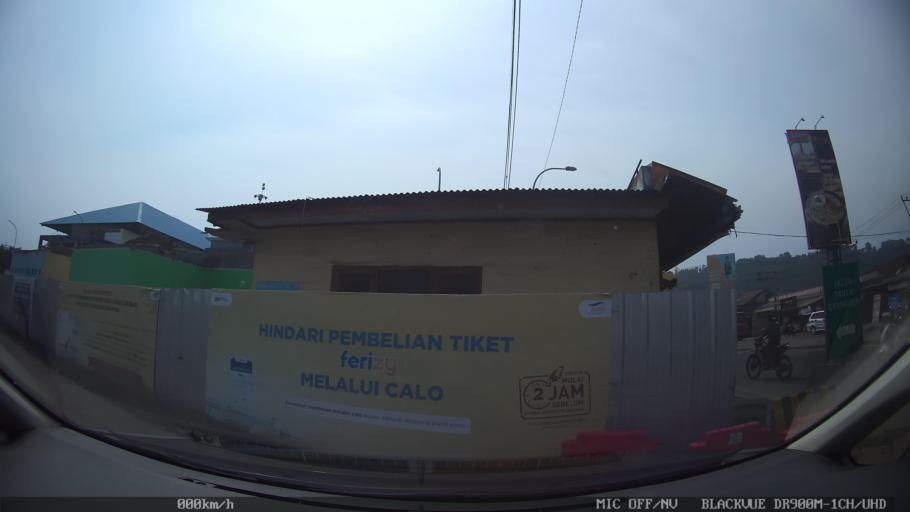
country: ID
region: Banten
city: Kubangkepuh
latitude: -5.9352
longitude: 106.0019
